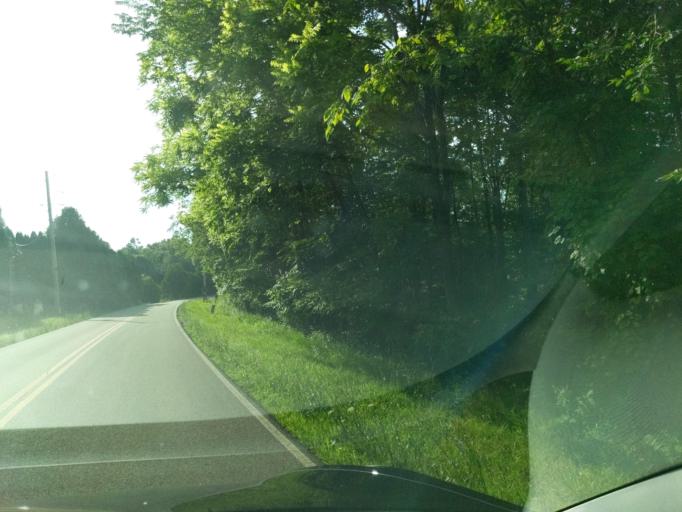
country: US
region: Ohio
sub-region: Fairfield County
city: Lancaster
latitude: 39.5496
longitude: -82.6327
